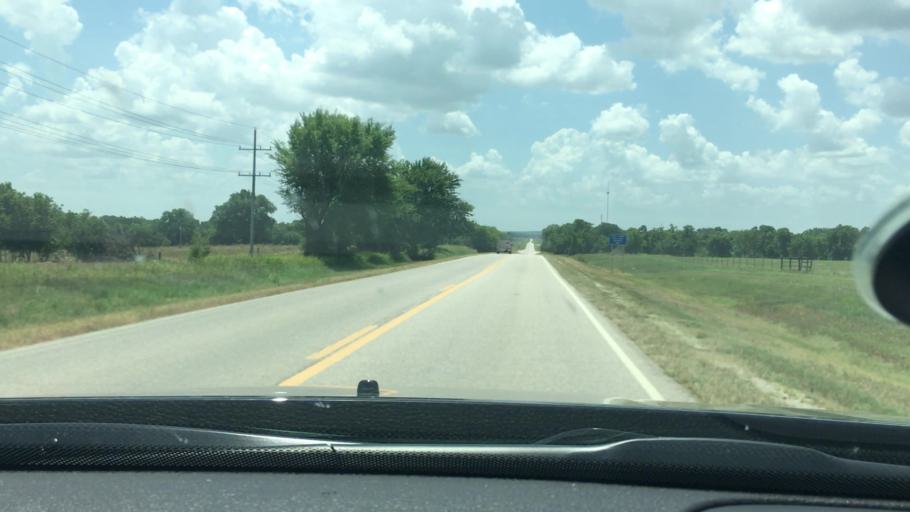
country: US
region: Oklahoma
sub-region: Pontotoc County
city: Ada
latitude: 34.6643
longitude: -96.6349
